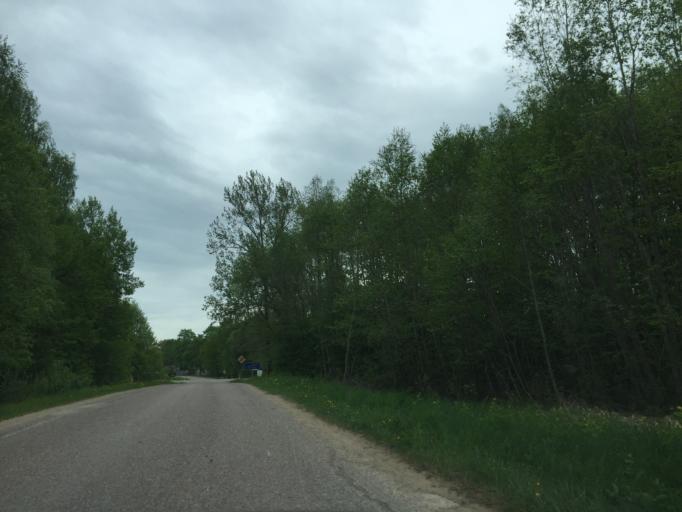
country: LV
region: Lielvarde
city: Lielvarde
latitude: 56.8019
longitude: 24.8642
